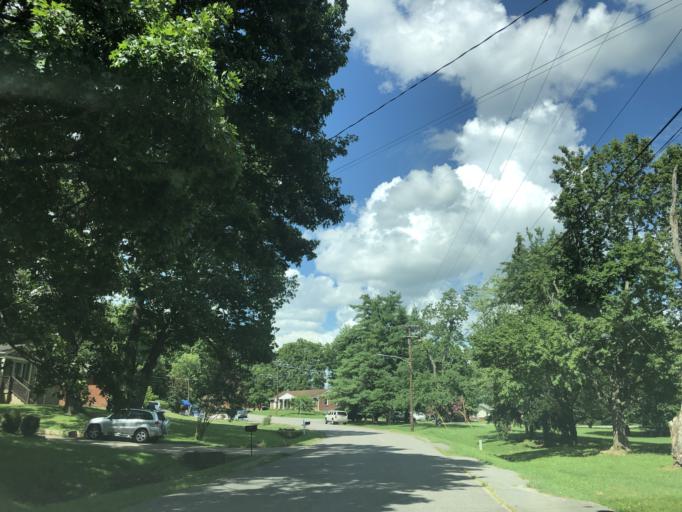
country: US
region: Tennessee
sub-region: Davidson County
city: Oak Hill
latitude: 36.0761
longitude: -86.7323
